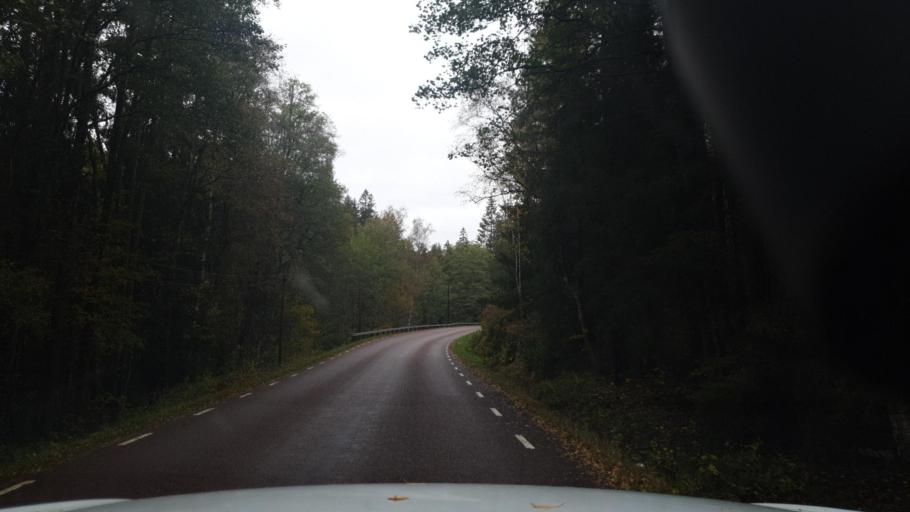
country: SE
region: Vaermland
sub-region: Grums Kommun
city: Grums
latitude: 59.4072
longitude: 13.0716
